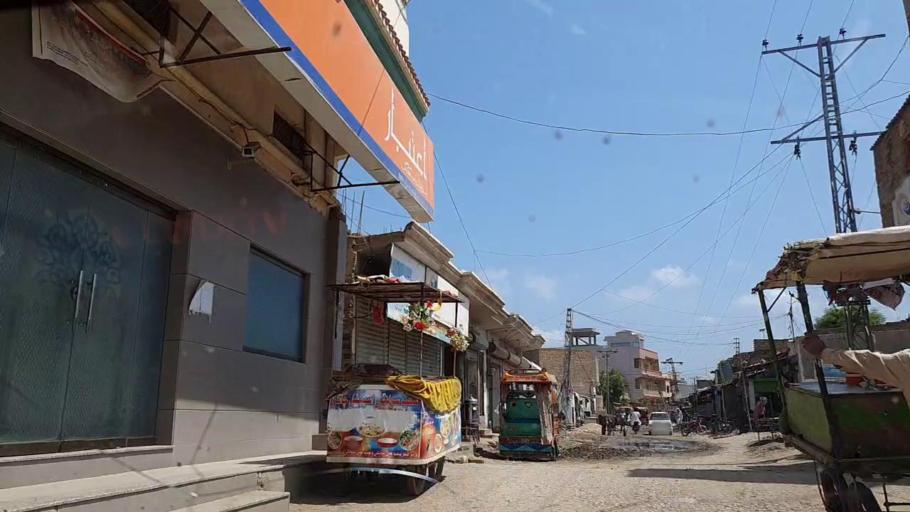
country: PK
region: Sindh
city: Tharu Shah
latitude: 26.9424
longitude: 68.1186
